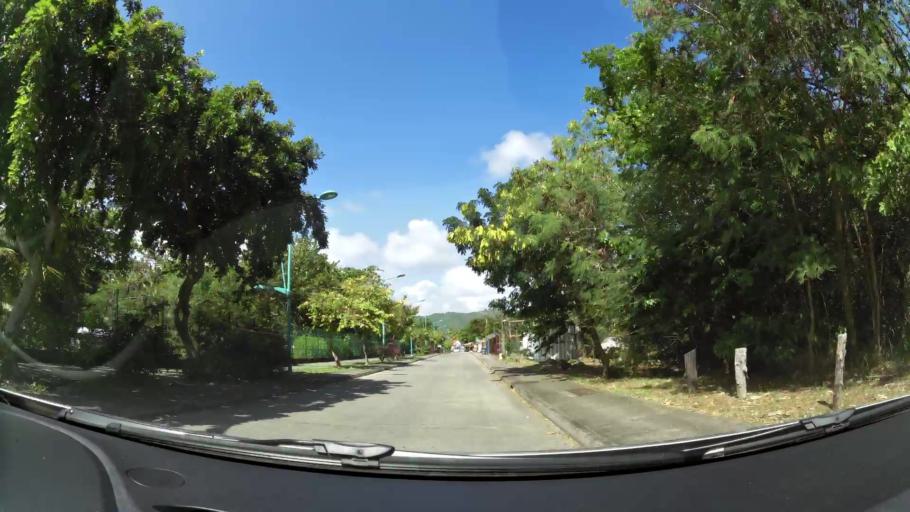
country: MQ
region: Martinique
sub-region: Martinique
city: Le Marin
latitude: 14.4427
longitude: -60.8794
